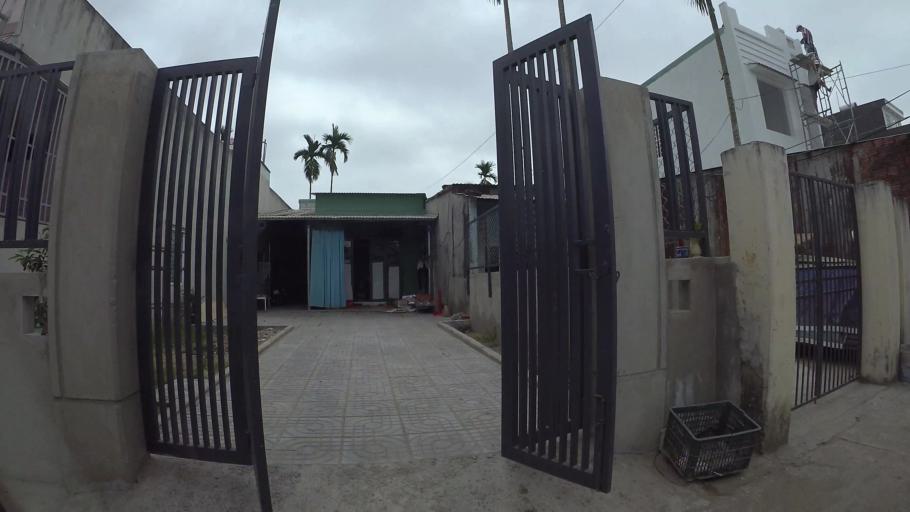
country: VN
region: Da Nang
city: Lien Chieu
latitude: 16.0409
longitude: 108.1716
